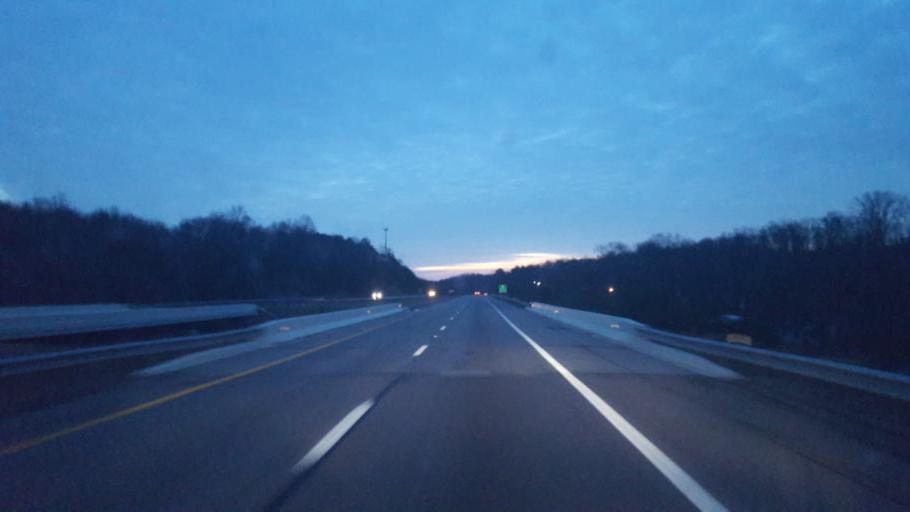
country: US
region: Ohio
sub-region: Jackson County
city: Jackson
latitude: 39.0828
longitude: -82.6394
